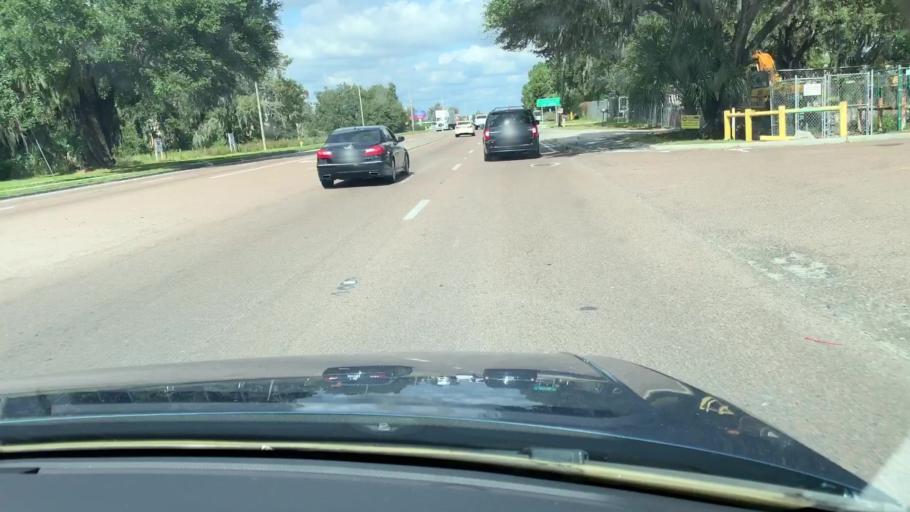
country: US
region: Florida
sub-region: Polk County
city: Winston
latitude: 28.0295
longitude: -82.0558
